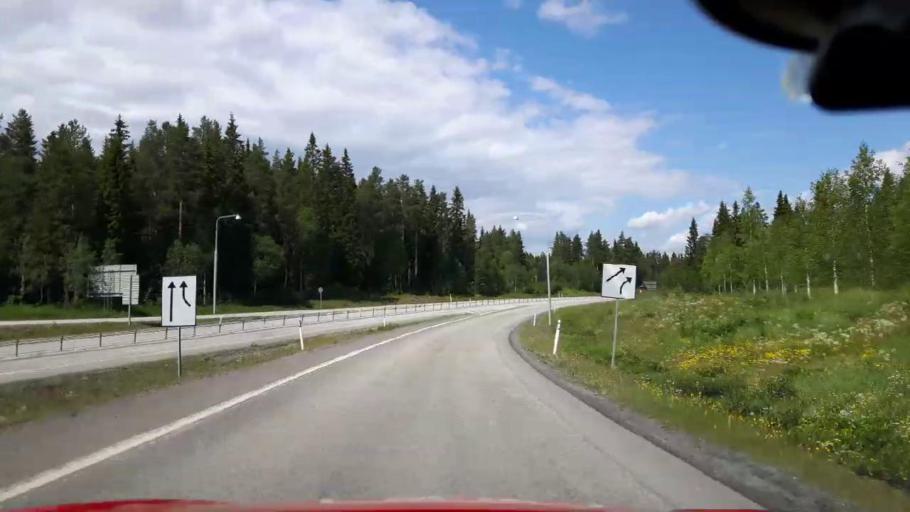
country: SE
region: Jaemtland
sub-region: OEstersunds Kommun
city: Ostersund
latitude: 63.1811
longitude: 14.6901
